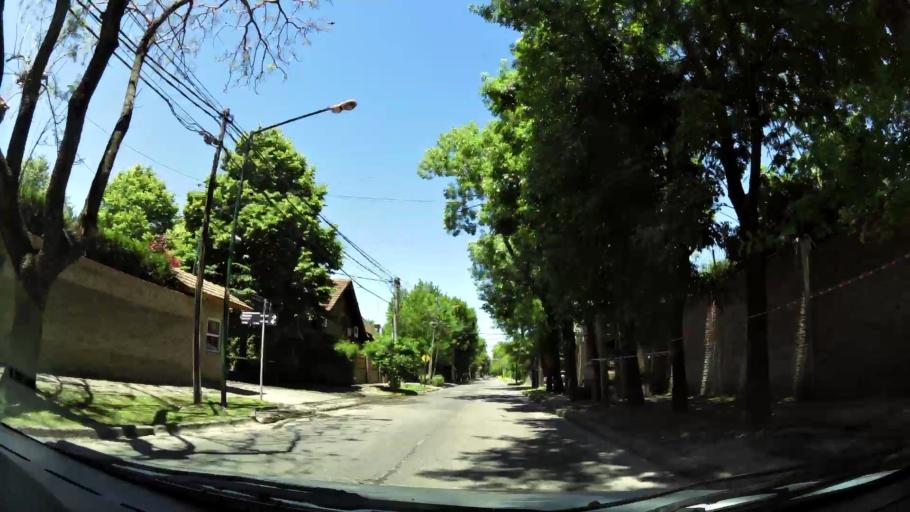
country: AR
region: Buenos Aires
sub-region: Partido de San Isidro
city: San Isidro
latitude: -34.4948
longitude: -58.5710
